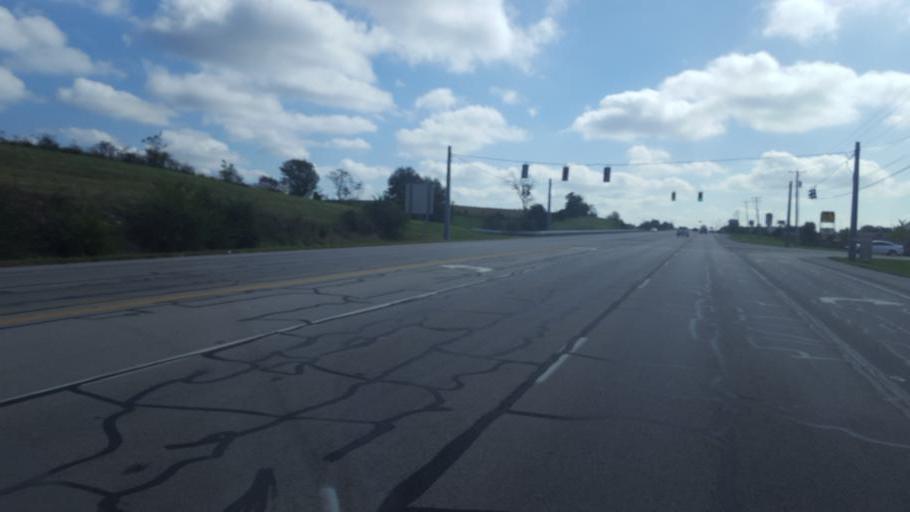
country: US
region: Ohio
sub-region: Brown County
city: Aberdeen
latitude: 38.6235
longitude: -83.7863
